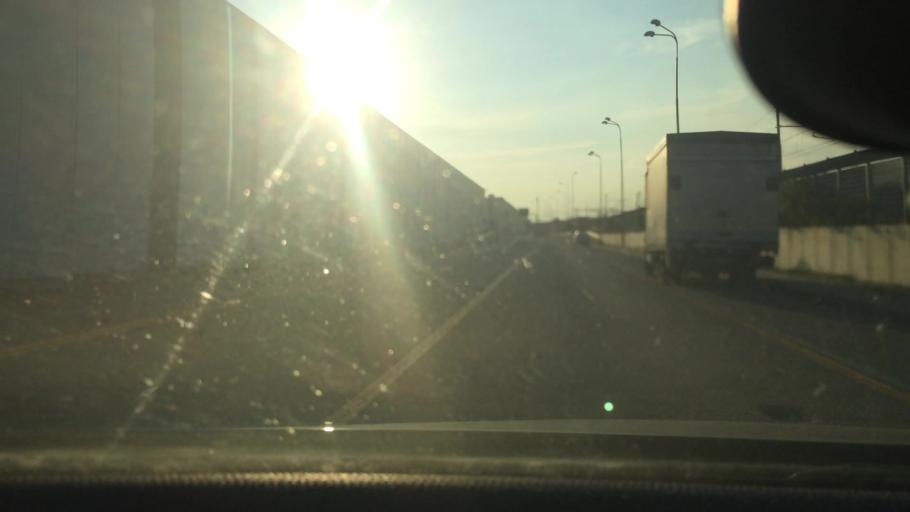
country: IT
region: Lombardy
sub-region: Citta metropolitana di Milano
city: Pero
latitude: 45.5225
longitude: 9.0830
